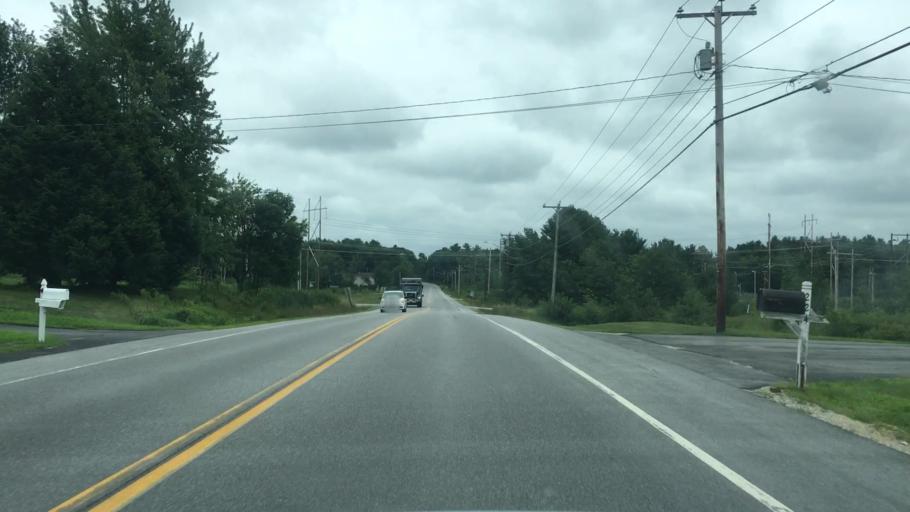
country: US
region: Maine
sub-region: York County
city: Biddeford
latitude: 43.5312
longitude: -70.5050
